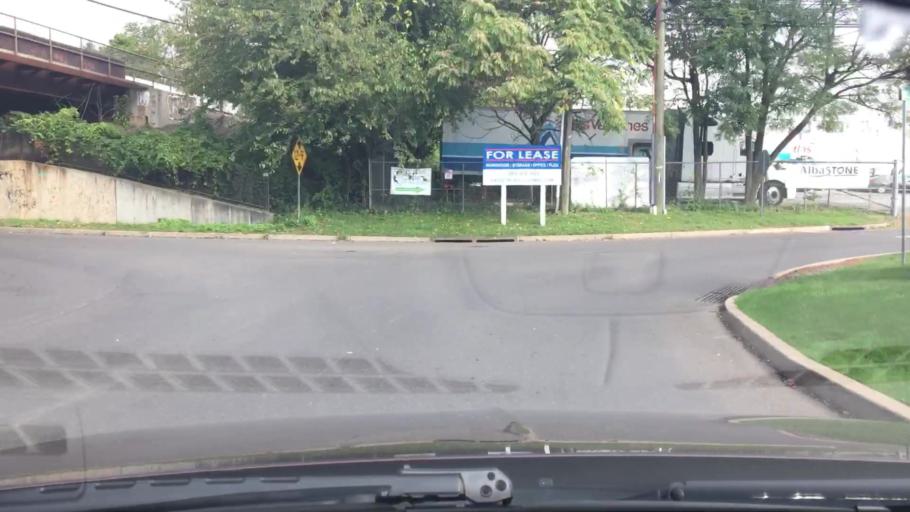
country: US
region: Connecticut
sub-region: Fairfield County
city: Stamford
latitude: 41.0797
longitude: -73.5204
